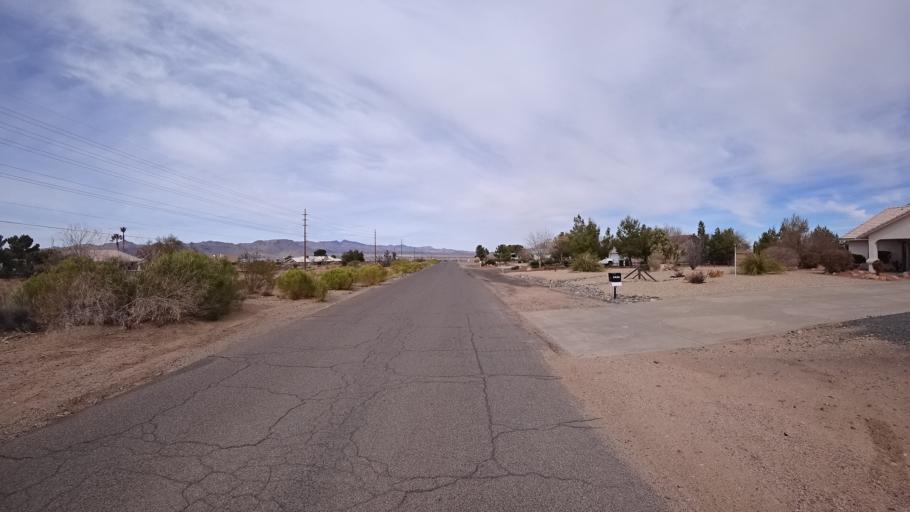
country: US
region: Arizona
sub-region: Mohave County
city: Kingman
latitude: 35.1935
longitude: -113.9860
